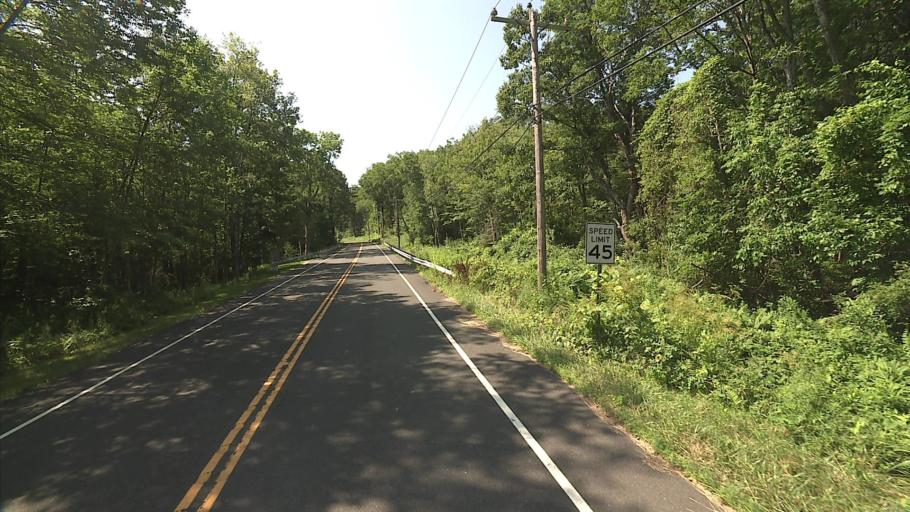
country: US
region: Massachusetts
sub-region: Berkshire County
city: New Marlborough
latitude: 42.0315
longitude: -73.2074
